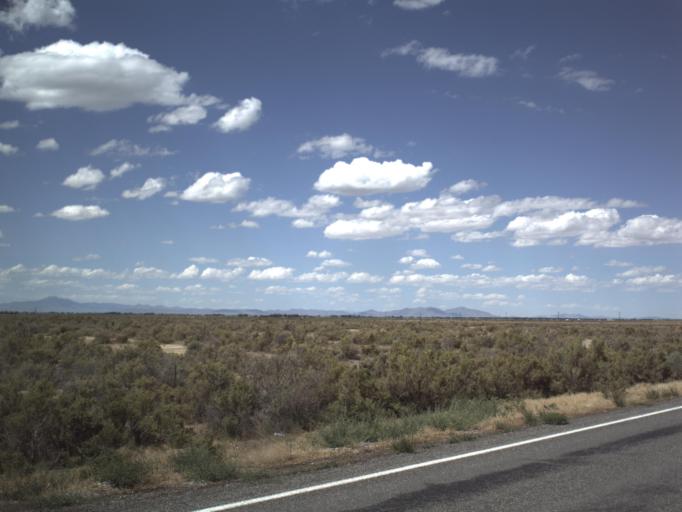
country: US
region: Utah
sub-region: Millard County
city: Delta
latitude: 39.2795
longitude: -112.4594
